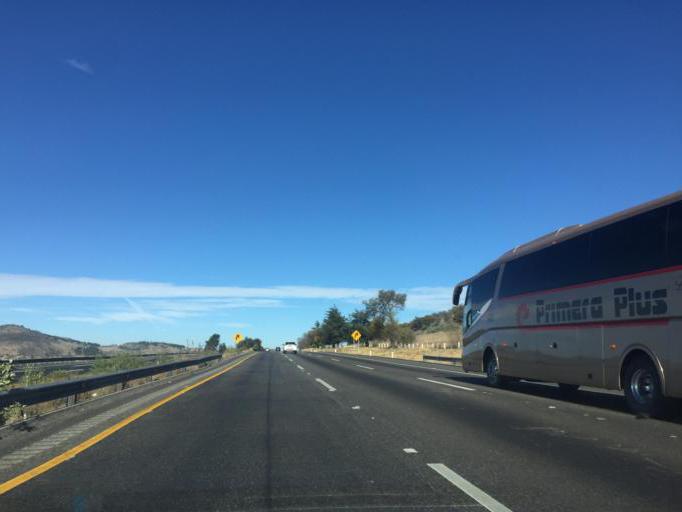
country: MX
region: Mexico
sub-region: Aculco
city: El Colorado
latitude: 20.1177
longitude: -99.7185
